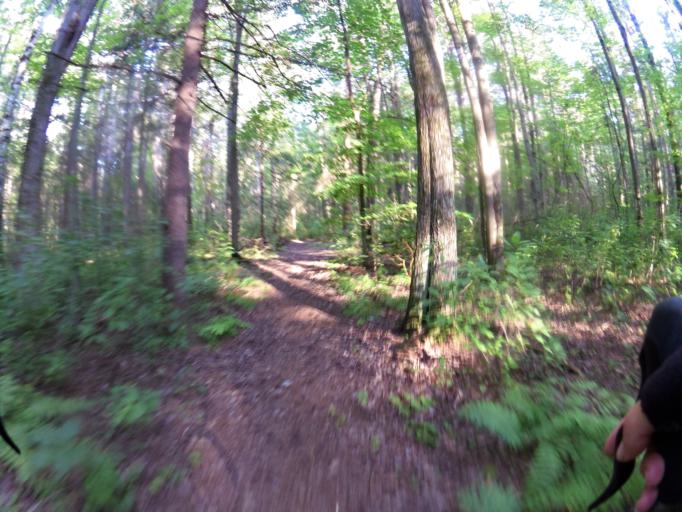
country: CA
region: Ontario
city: Bells Corners
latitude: 45.3194
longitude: -75.7334
